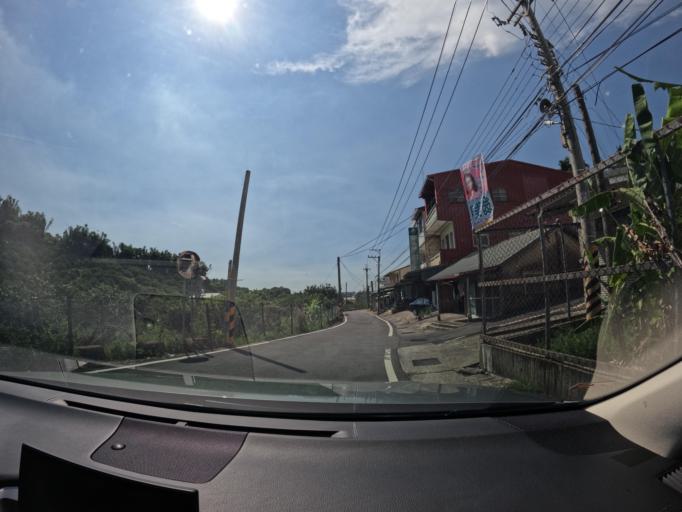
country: TW
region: Taiwan
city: Fengyuan
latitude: 24.3123
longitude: 120.7458
